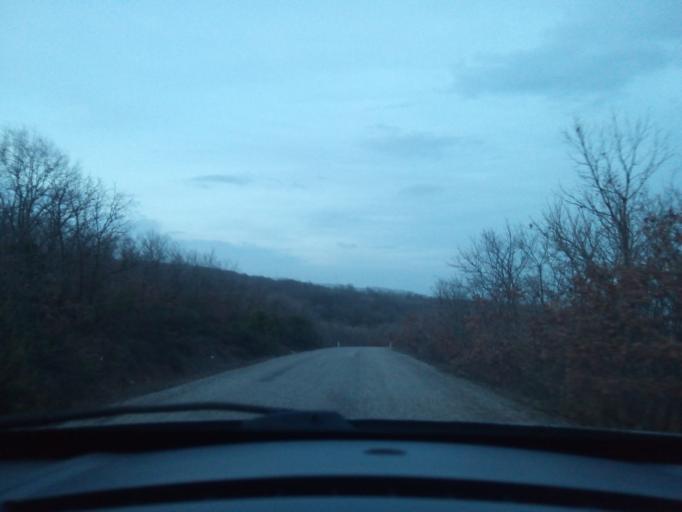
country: TR
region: Balikesir
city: Omerkoy
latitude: 39.9109
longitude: 28.0478
